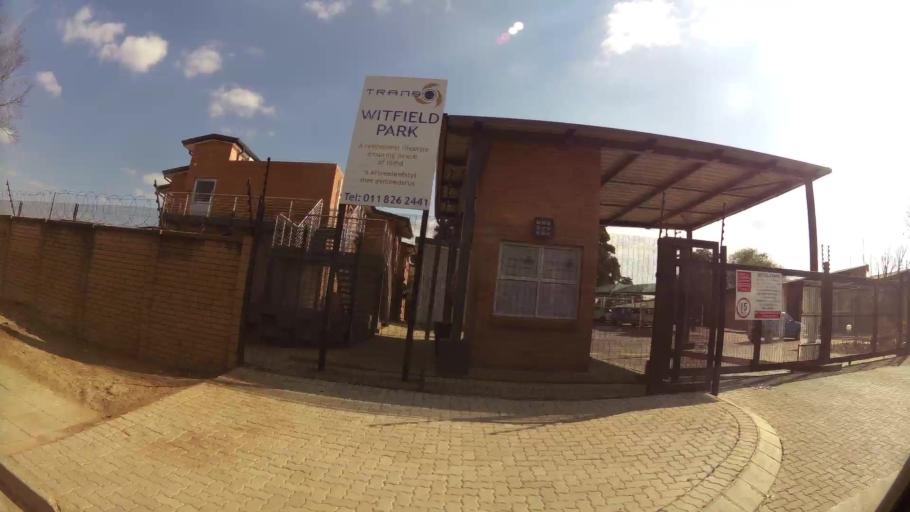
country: ZA
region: Gauteng
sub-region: Ekurhuleni Metropolitan Municipality
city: Germiston
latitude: -26.1829
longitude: 28.2028
